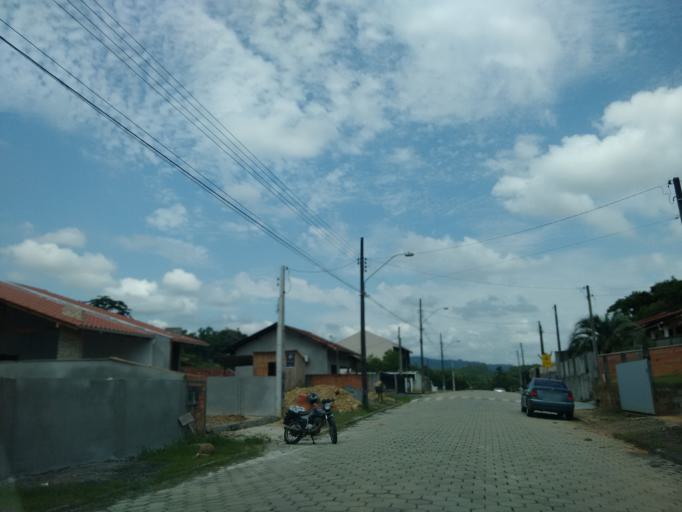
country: BR
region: Santa Catarina
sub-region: Blumenau
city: Blumenau
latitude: -26.8626
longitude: -49.1392
